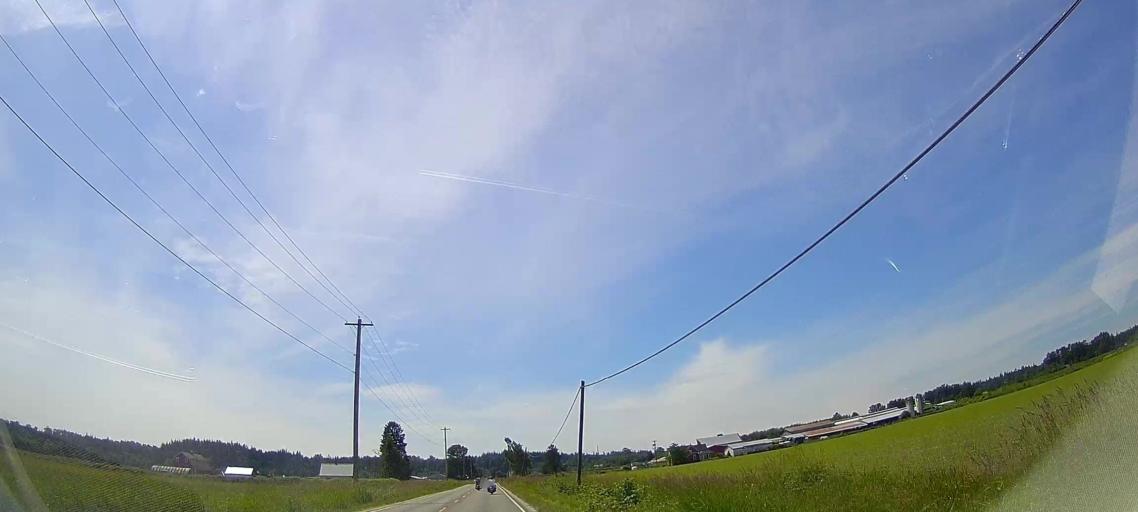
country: US
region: Washington
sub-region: Snohomish County
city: Smokey Point
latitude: 48.1880
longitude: -122.2137
